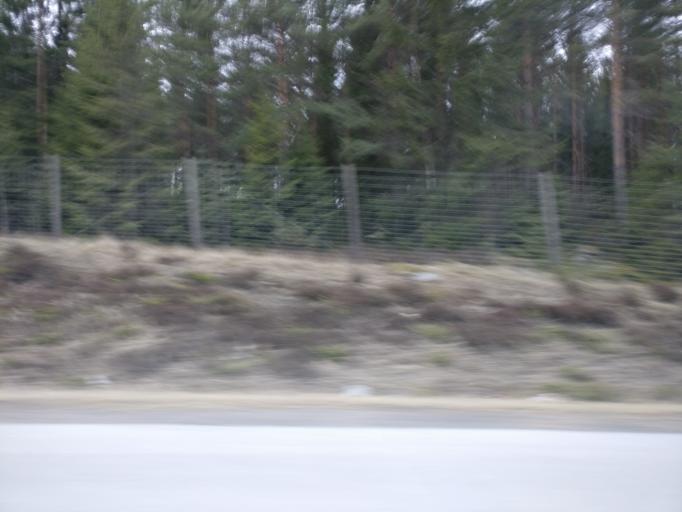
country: FI
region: Haeme
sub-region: Haemeenlinna
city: Janakkala
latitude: 60.9210
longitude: 24.5284
